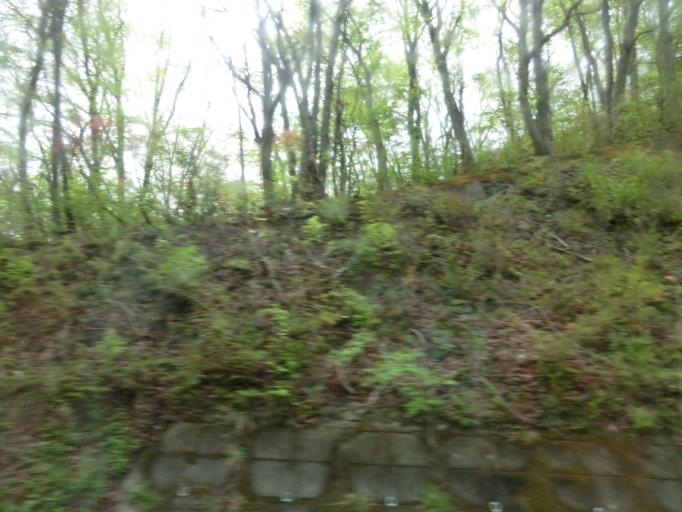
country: JP
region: Iwate
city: Otsuchi
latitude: 39.3927
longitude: 141.9449
